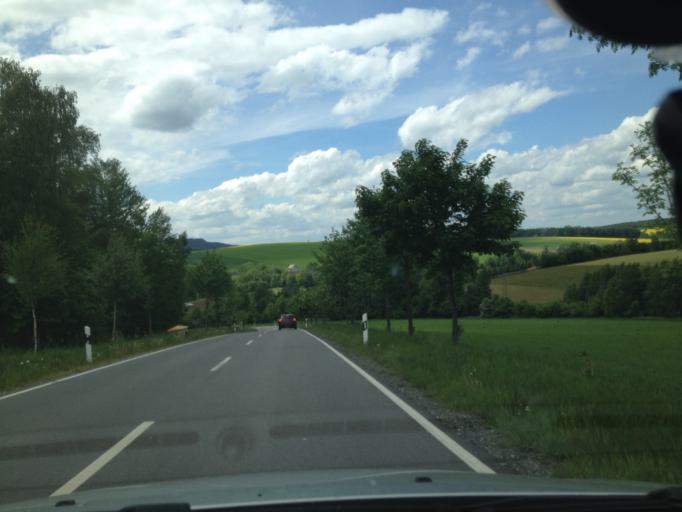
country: DE
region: Saxony
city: Barenstein
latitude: 50.5204
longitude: 13.0026
